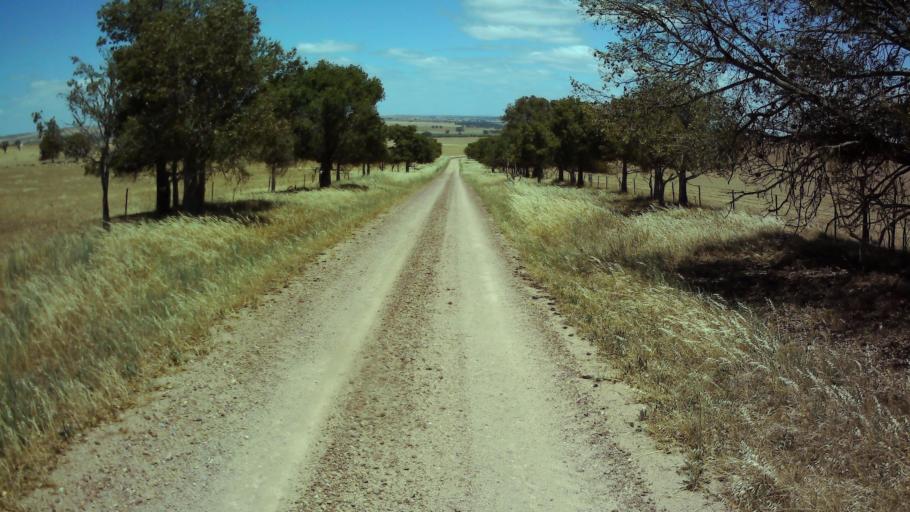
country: AU
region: New South Wales
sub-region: Weddin
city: Grenfell
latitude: -33.9612
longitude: 148.3646
